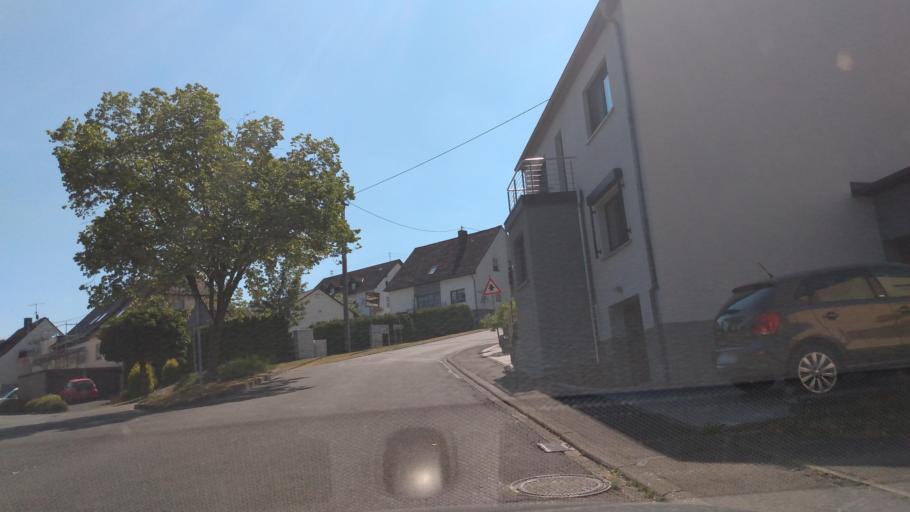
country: DE
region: Rheinland-Pfalz
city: Morbach
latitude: 49.8180
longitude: 7.1513
